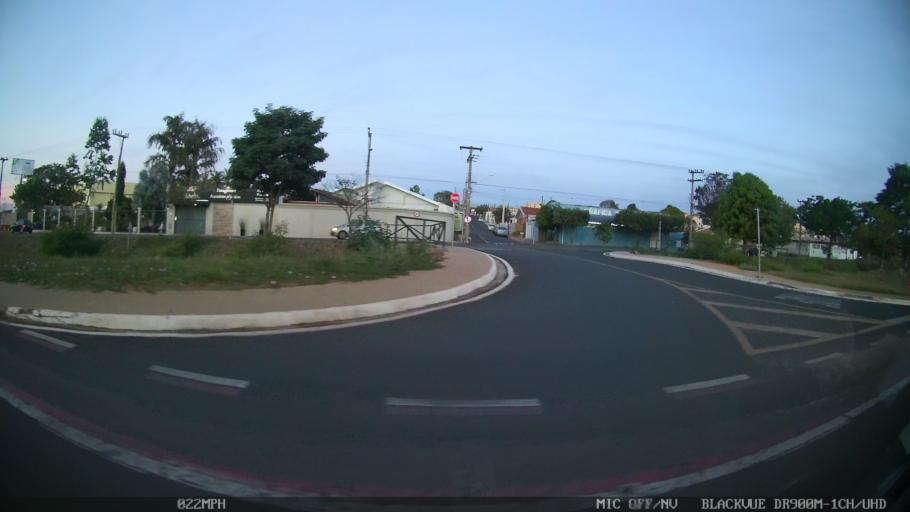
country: BR
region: Sao Paulo
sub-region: Catanduva
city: Catanduva
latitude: -21.1350
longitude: -48.9897
